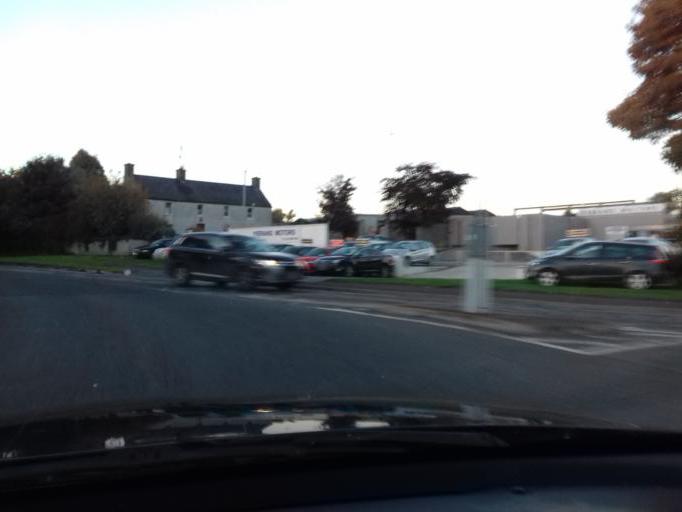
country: IE
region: Leinster
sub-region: Lu
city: Tullyallen
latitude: 53.7276
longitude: -6.3853
